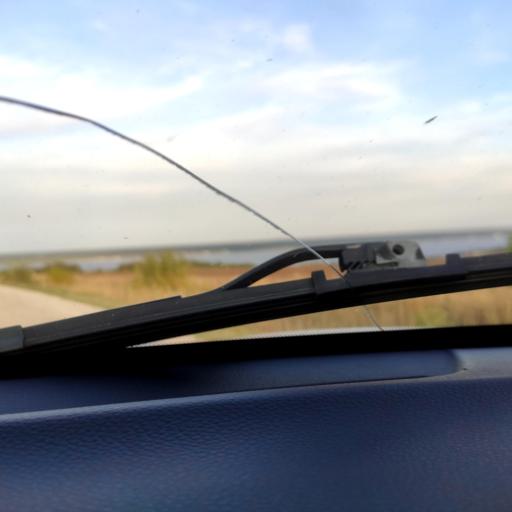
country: RU
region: Tatarstan
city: Verkhniy Uslon
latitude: 55.6474
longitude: 48.9323
